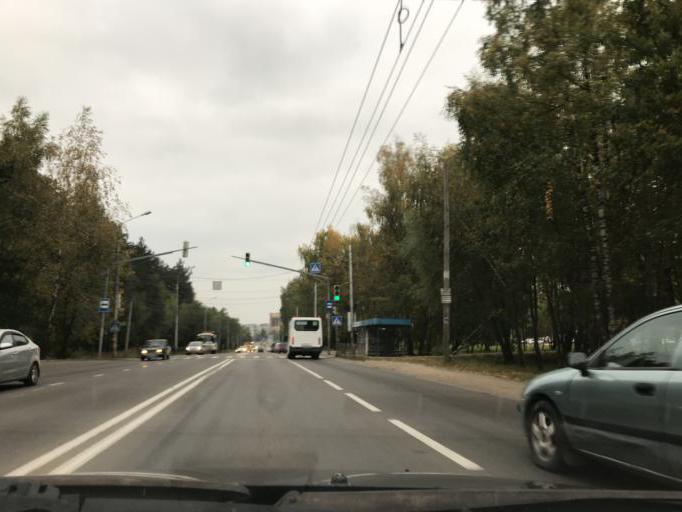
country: RU
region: Kaluga
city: Kaluga
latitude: 54.5916
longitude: 36.2563
